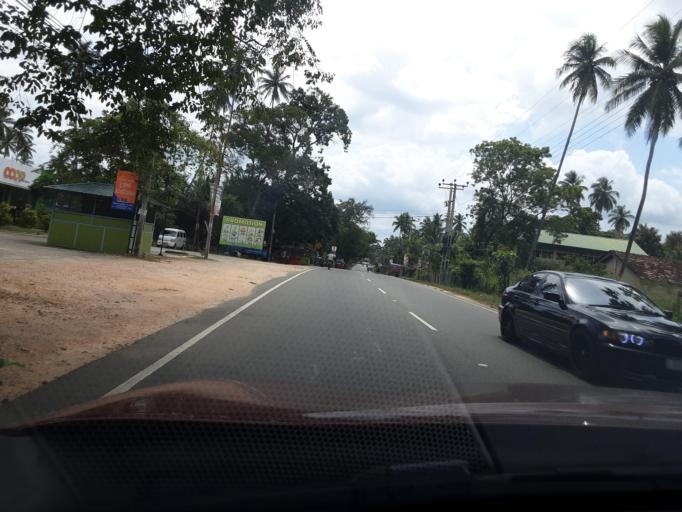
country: LK
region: North Western
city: Kuliyapitiya
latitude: 7.4513
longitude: 80.1840
